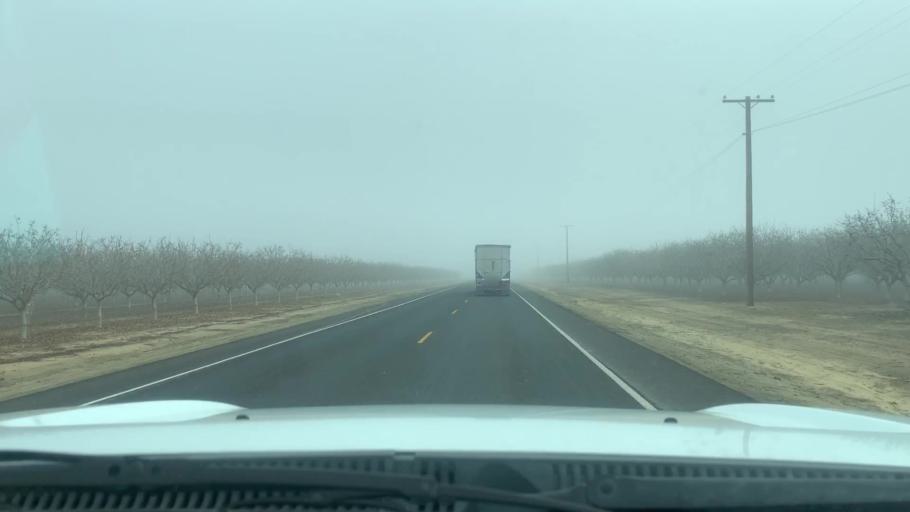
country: US
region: California
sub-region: Kern County
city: Lost Hills
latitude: 35.4993
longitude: -119.6314
